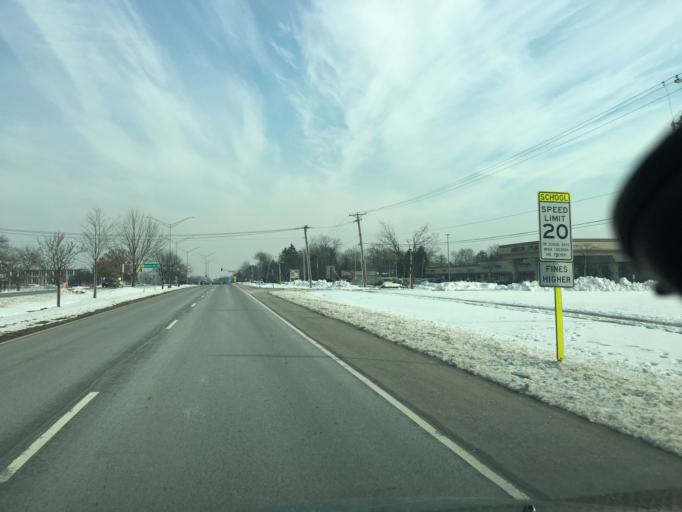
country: US
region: Illinois
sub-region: DuPage County
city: Darien
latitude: 41.7520
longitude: -87.9577
